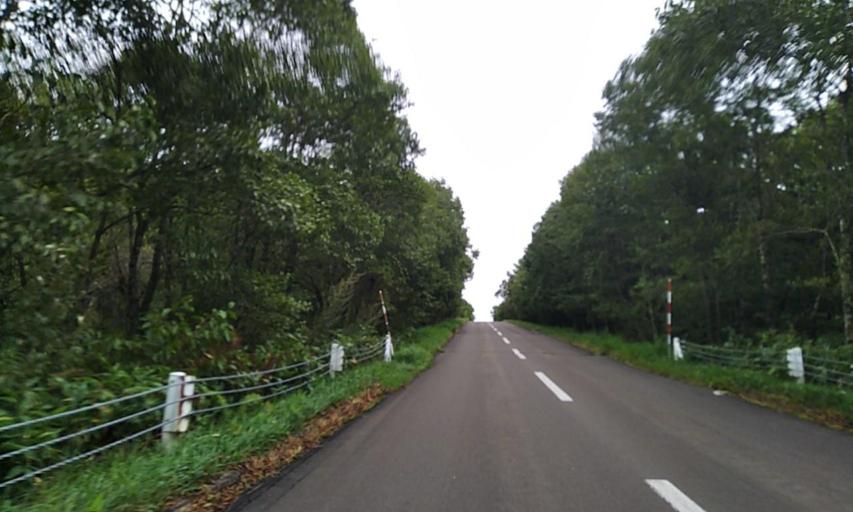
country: JP
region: Hokkaido
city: Nemuro
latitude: 43.2689
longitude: 145.2663
